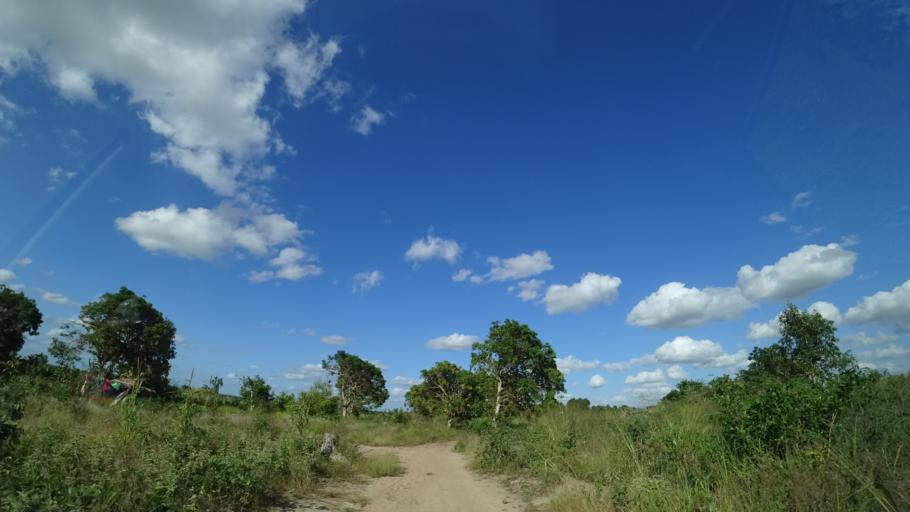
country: MZ
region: Sofala
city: Dondo
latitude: -19.4311
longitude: 34.7298
